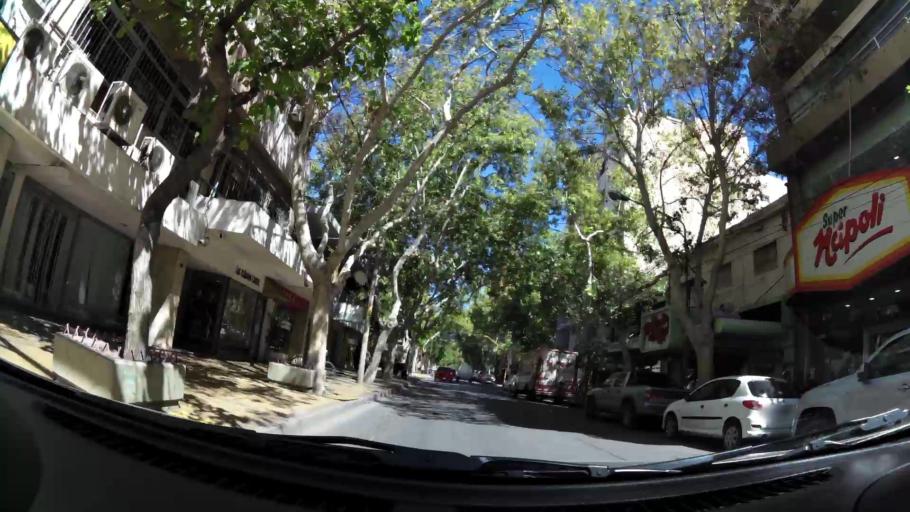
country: AR
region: San Juan
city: San Juan
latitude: -31.5369
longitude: -68.5281
